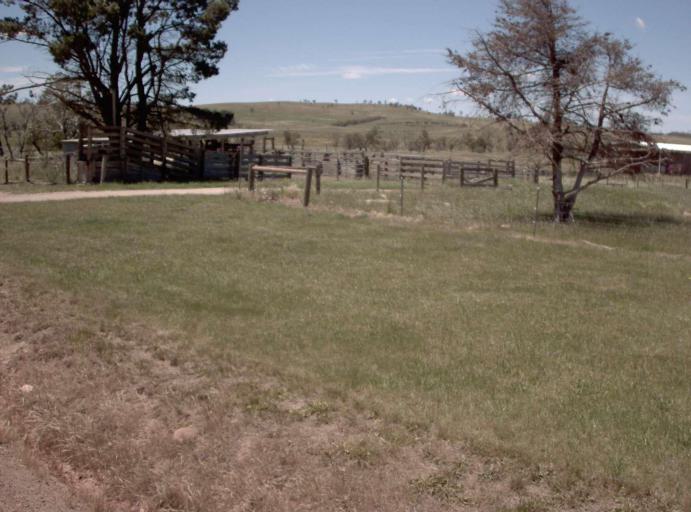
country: AU
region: New South Wales
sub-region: Snowy River
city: Jindabyne
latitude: -37.0141
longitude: 148.2785
